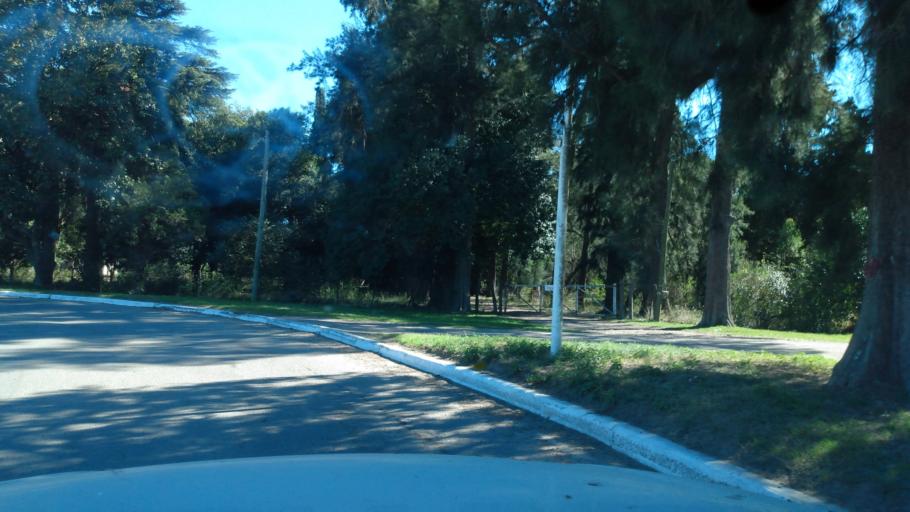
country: AR
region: Buenos Aires
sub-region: Partido de Lujan
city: Lujan
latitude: -34.5554
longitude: -59.0984
